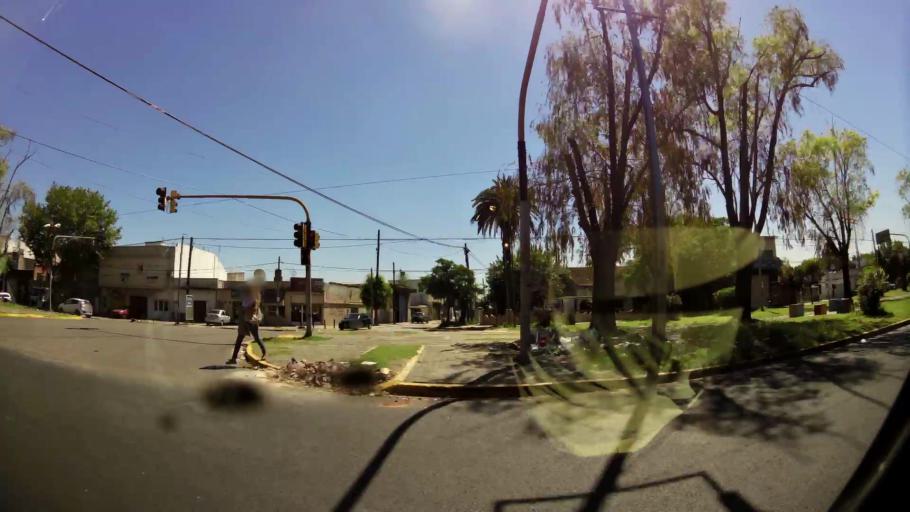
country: AR
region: Buenos Aires
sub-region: Partido de Quilmes
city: Quilmes
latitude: -34.7122
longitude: -58.3054
